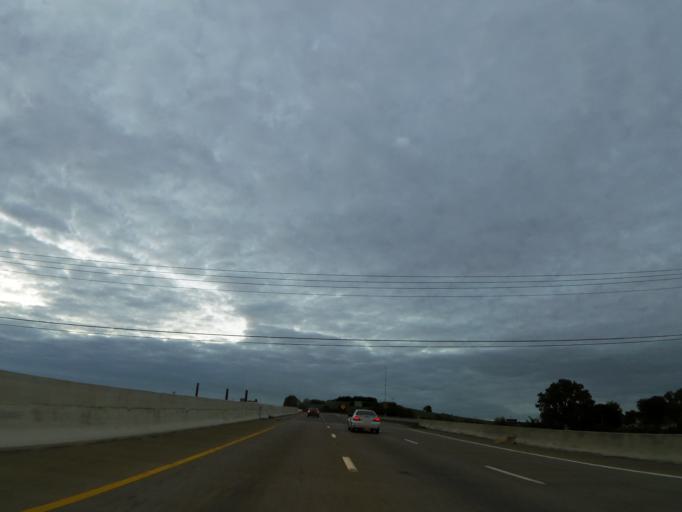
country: US
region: Tennessee
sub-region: Davidson County
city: Belle Meade
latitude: 36.1713
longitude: -86.8692
